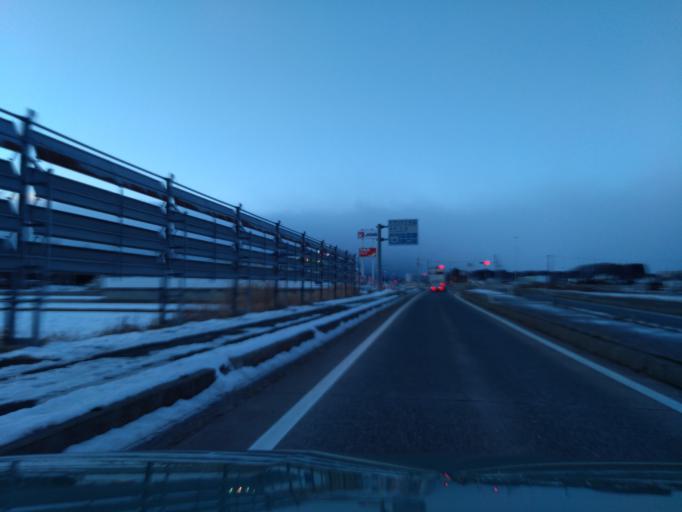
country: JP
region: Iwate
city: Shizukuishi
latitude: 39.6947
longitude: 140.9799
